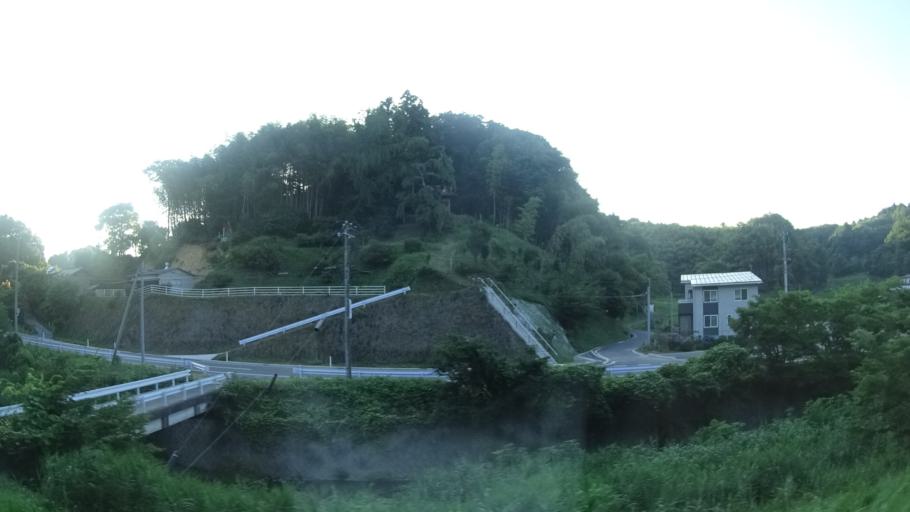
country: JP
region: Fukushima
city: Miharu
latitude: 37.4476
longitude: 140.4697
